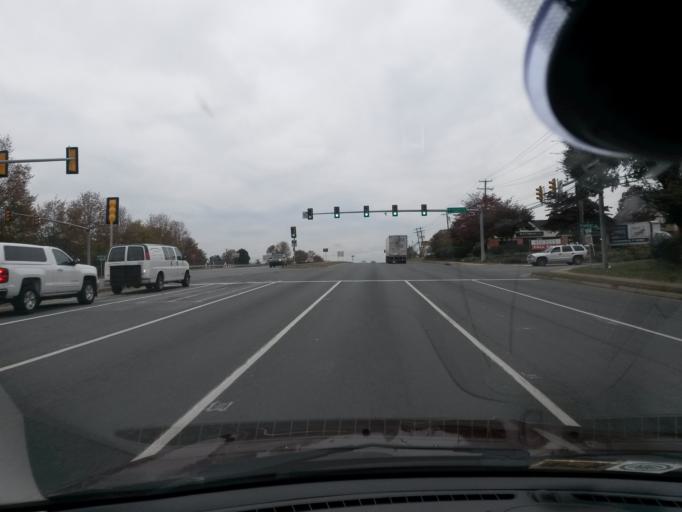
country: US
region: Virginia
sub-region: City of Charlottesville
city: Charlottesville
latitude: 38.0744
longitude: -78.4807
